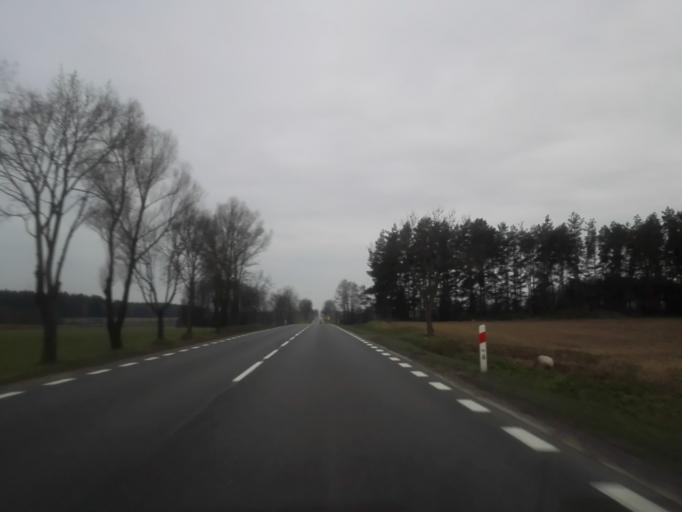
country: PL
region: Podlasie
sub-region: Powiat kolnenski
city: Stawiski
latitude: 53.4717
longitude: 22.2060
